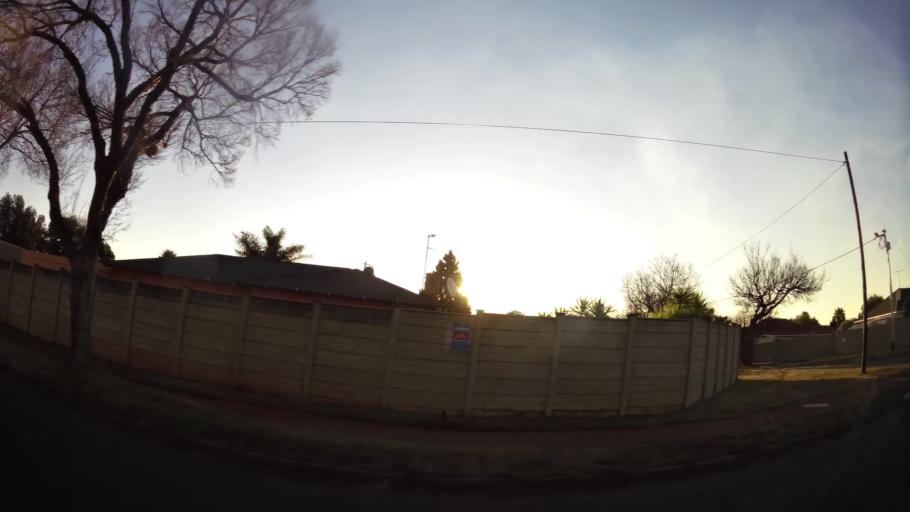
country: ZA
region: Gauteng
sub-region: City of Johannesburg Metropolitan Municipality
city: Roodepoort
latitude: -26.1543
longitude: 27.8772
